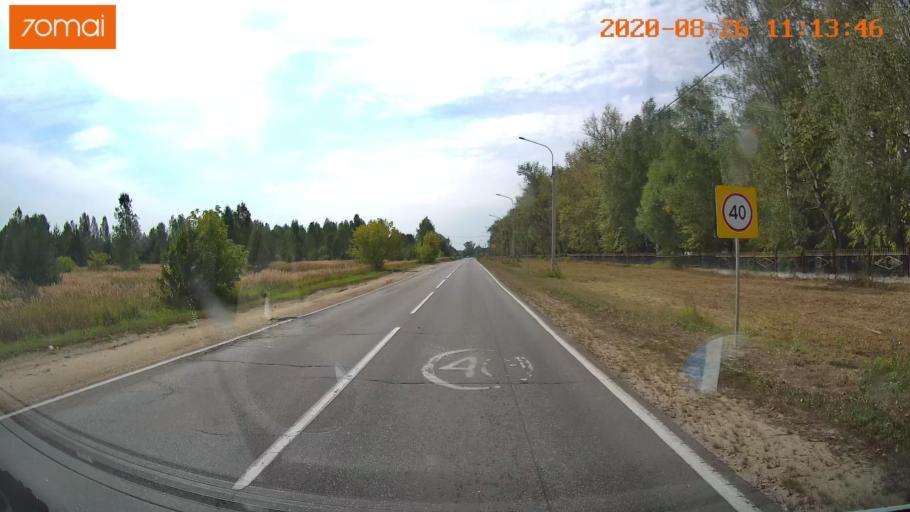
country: RU
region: Rjazan
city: Izhevskoye
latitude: 54.4535
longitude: 41.1188
